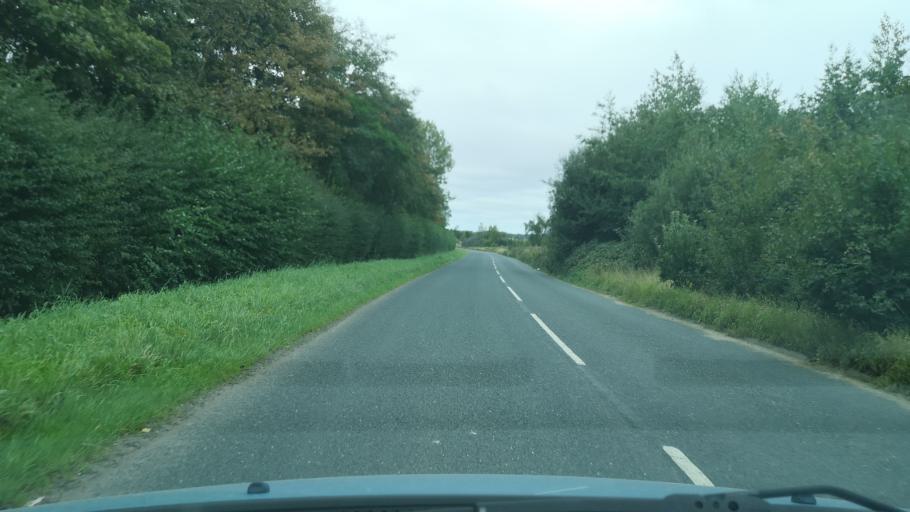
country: GB
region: England
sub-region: Doncaster
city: Norton
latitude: 53.6932
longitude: -1.1933
